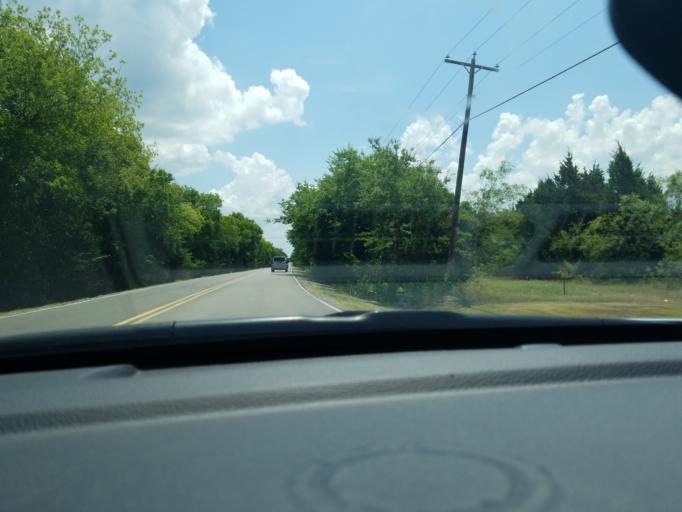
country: US
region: Texas
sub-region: Dallas County
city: Sunnyvale
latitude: 32.8140
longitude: -96.5912
